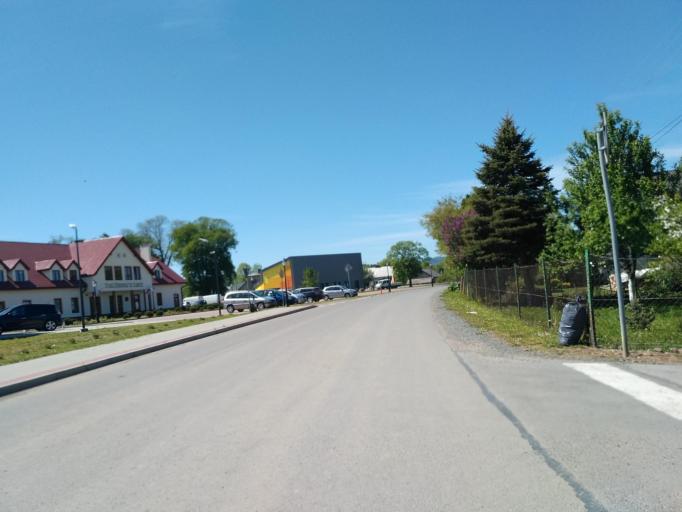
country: PL
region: Subcarpathian Voivodeship
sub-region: Powiat sanocki
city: Besko
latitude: 49.5945
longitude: 21.9648
